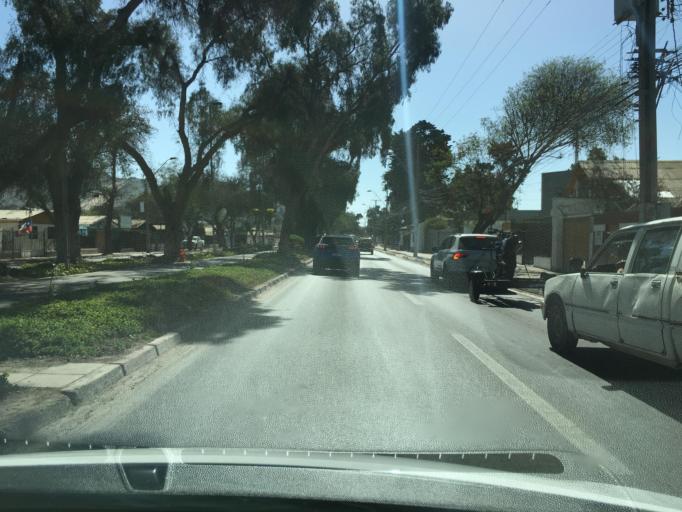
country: CL
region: Atacama
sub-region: Provincia de Copiapo
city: Copiapo
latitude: -27.3762
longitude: -70.3234
